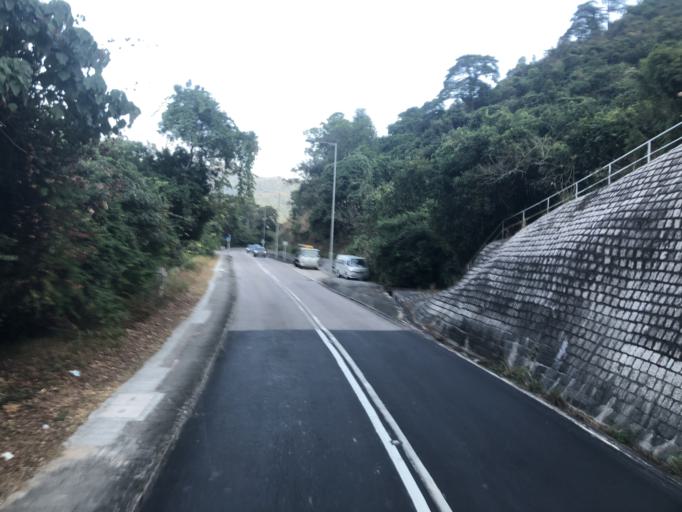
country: HK
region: Sai Kung
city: Sai Kung
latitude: 22.4153
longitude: 114.2662
